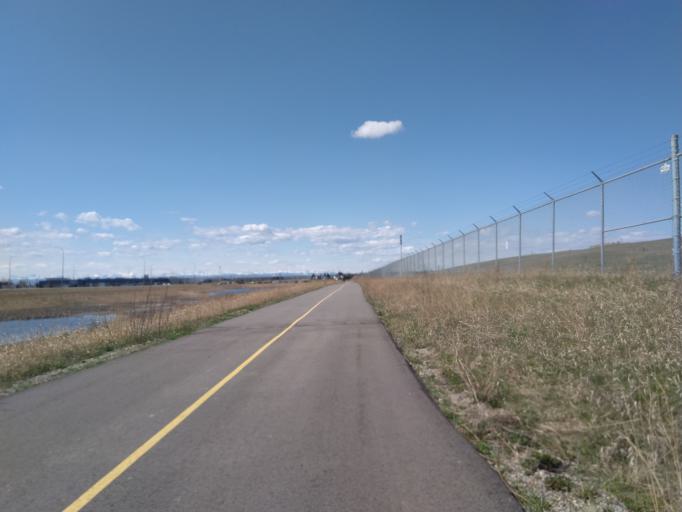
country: CA
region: Alberta
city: Chestermere
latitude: 51.0160
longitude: -113.9499
